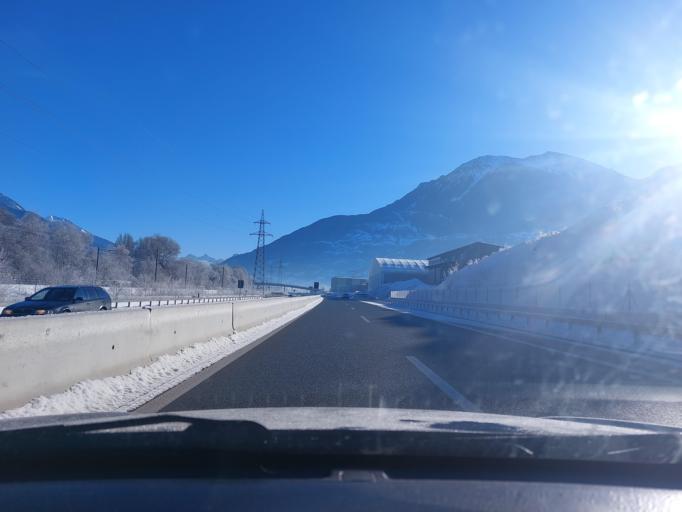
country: CH
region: Valais
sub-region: Leuk District
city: Leuk
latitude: 46.3064
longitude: 7.6635
